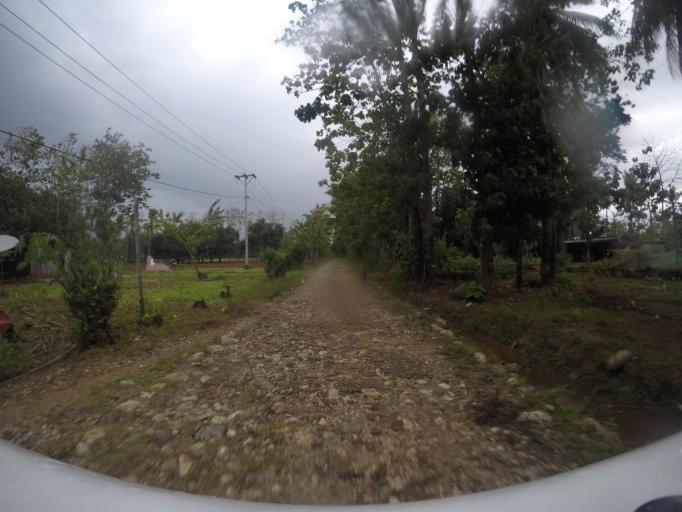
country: TL
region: Bobonaro
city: Maliana
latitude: -8.9619
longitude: 125.2143
